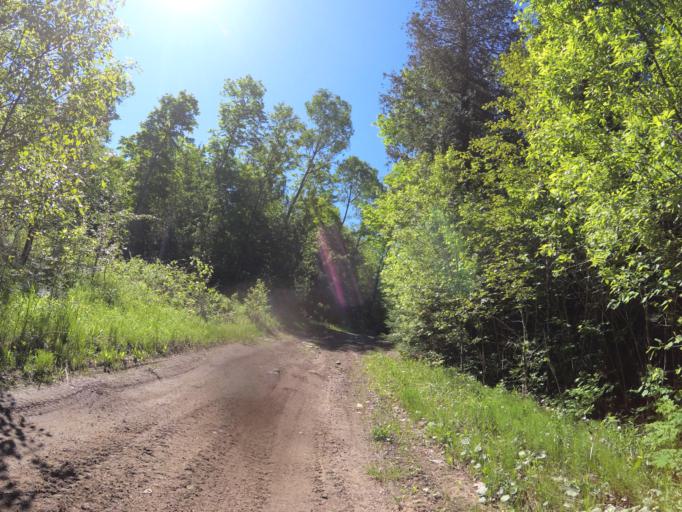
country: CA
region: Ontario
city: Renfrew
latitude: 45.0855
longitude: -77.0931
